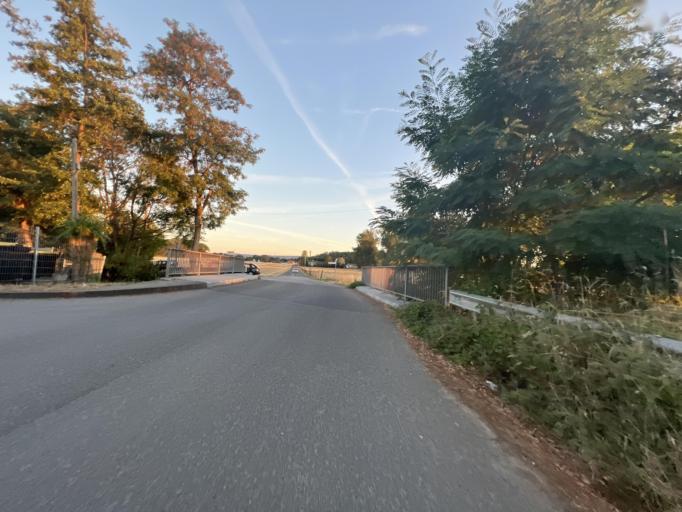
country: DE
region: North Rhine-Westphalia
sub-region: Regierungsbezirk Koln
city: Langerwehe
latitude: 50.8175
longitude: 6.4208
